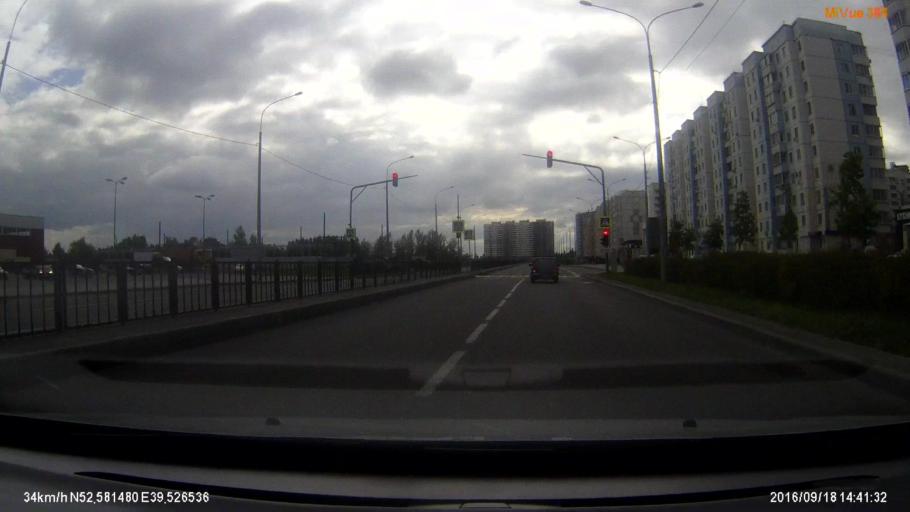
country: RU
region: Lipetsk
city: Syrskoye
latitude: 52.5815
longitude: 39.5266
